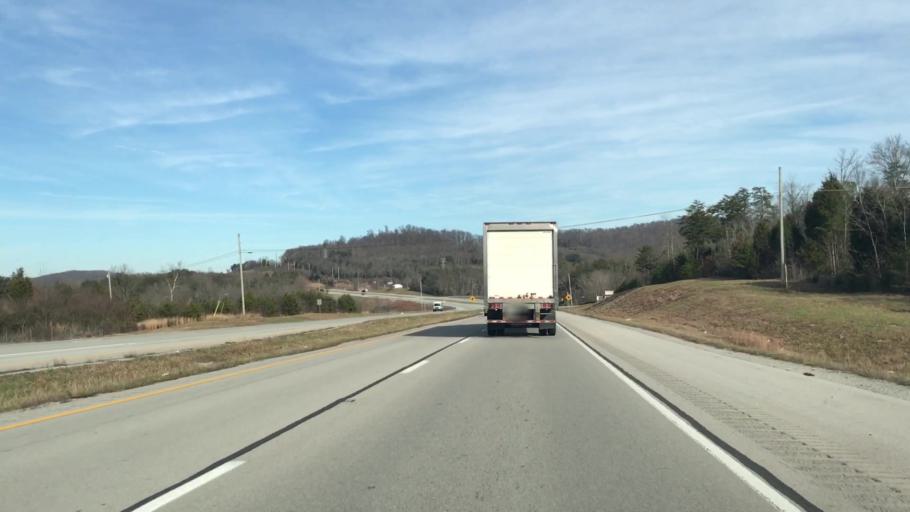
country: US
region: Kentucky
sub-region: Pulaski County
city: Somerset
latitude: 37.0186
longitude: -84.5971
